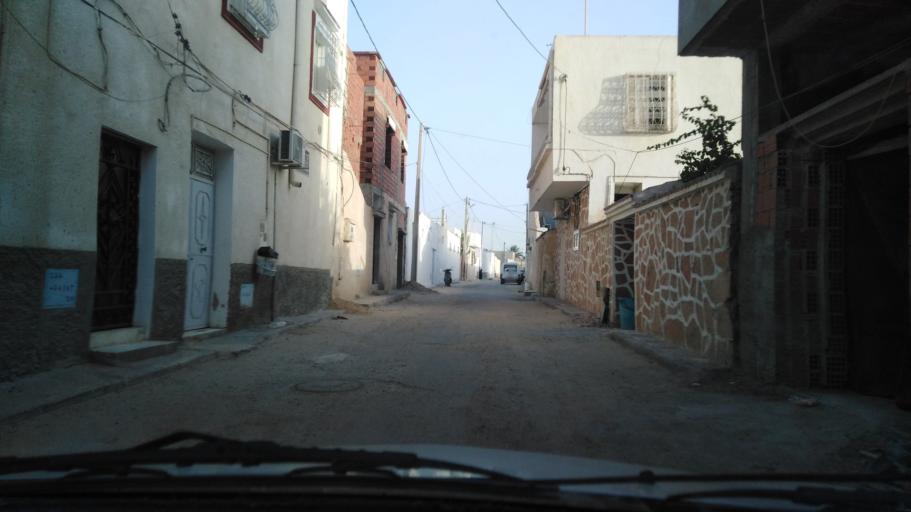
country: TN
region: Qabis
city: Gabes
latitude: 33.9592
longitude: 9.9968
